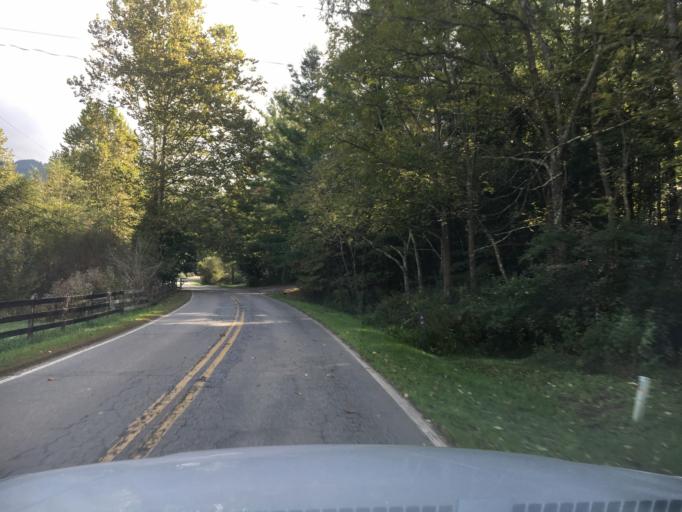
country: US
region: North Carolina
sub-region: Buncombe County
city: Swannanoa
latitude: 35.6067
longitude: -82.4258
